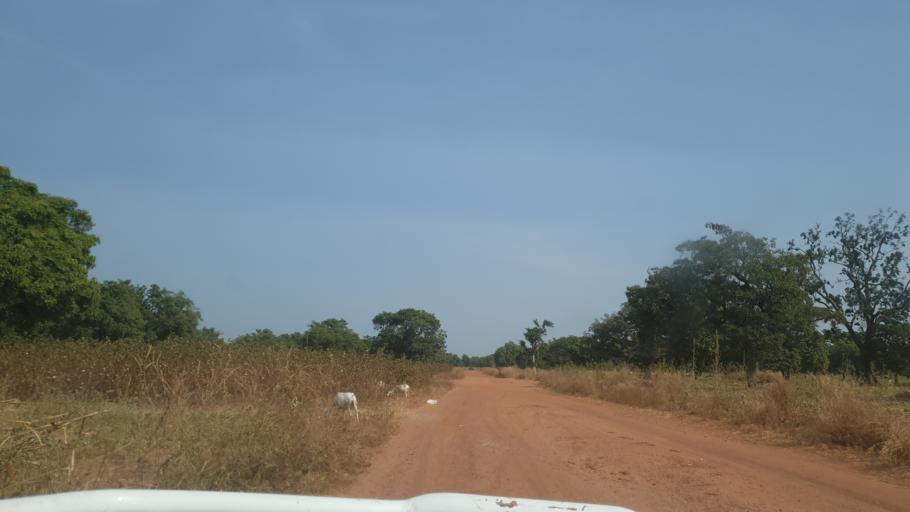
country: ML
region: Koulikoro
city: Dioila
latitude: 12.2288
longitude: -6.2206
